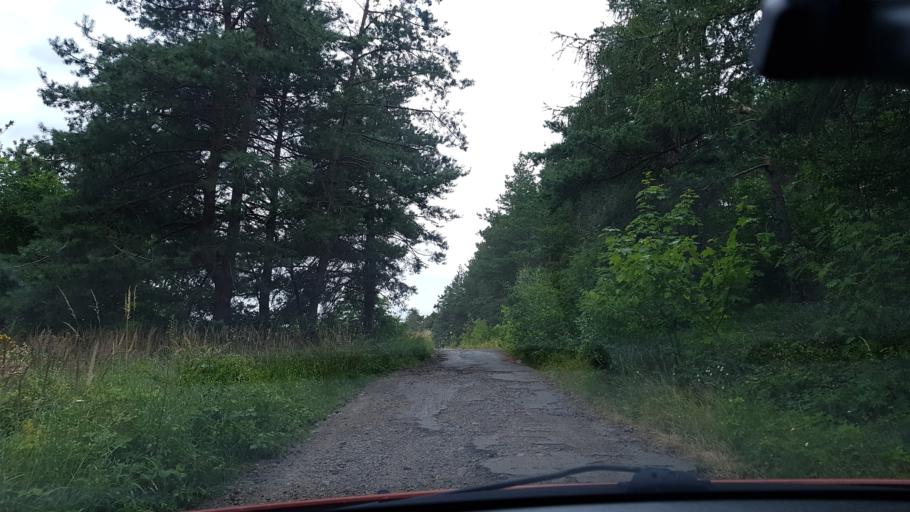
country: PL
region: Lower Silesian Voivodeship
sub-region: Powiat zabkowicki
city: Stoszowice
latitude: 50.5604
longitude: 16.7589
